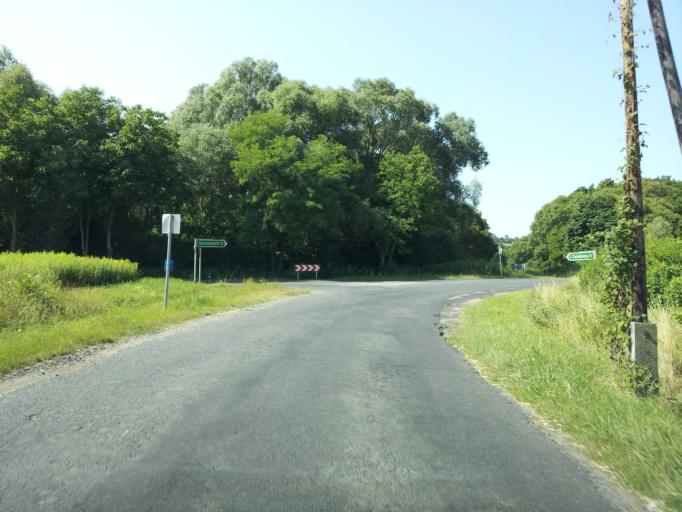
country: HU
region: Zala
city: Heviz
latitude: 46.8577
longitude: 17.1344
